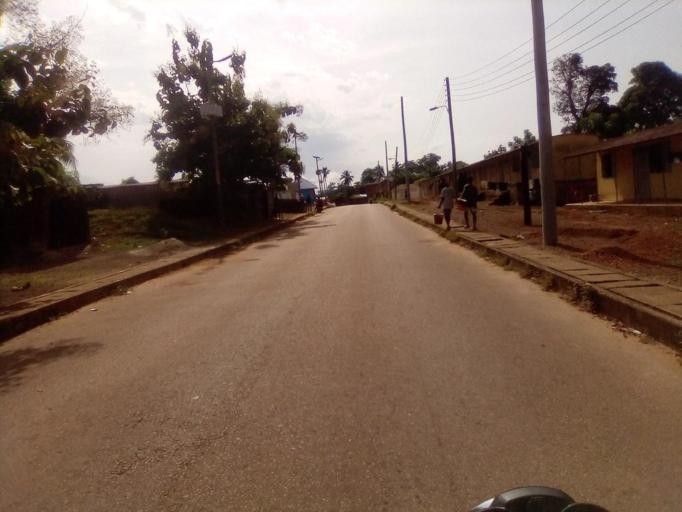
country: SL
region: Southern Province
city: Pujehun
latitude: 7.3573
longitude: -11.7172
